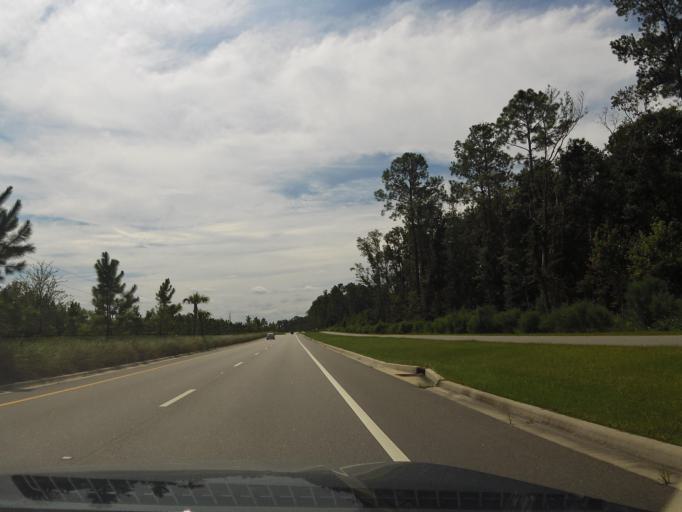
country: US
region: Florida
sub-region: Saint Johns County
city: Fruit Cove
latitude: 30.0467
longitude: -81.5298
